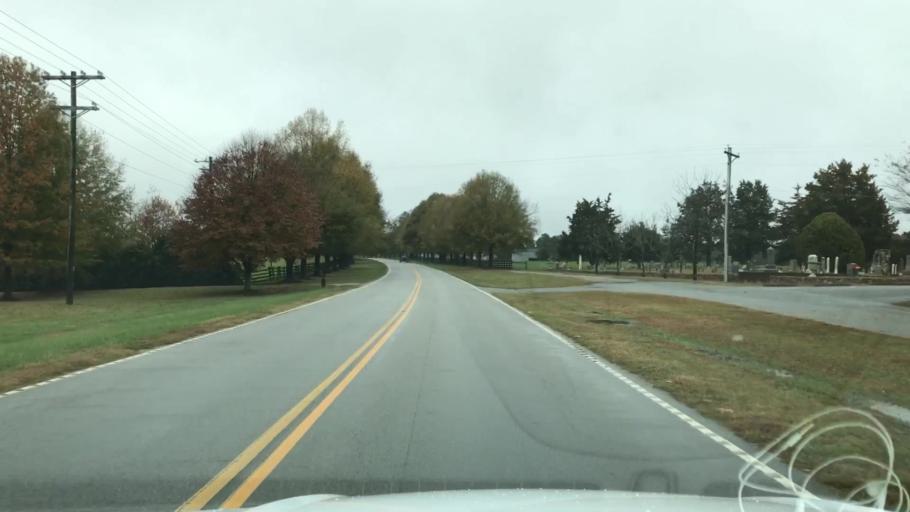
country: US
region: South Carolina
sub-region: Spartanburg County
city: Roebuck
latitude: 34.8067
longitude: -81.9184
